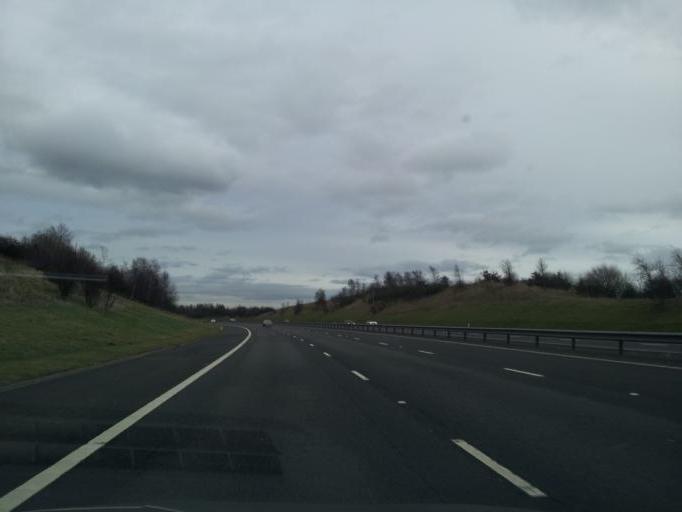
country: GB
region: England
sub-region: Staffordshire
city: Chasetown
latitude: 52.6505
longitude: -1.8883
